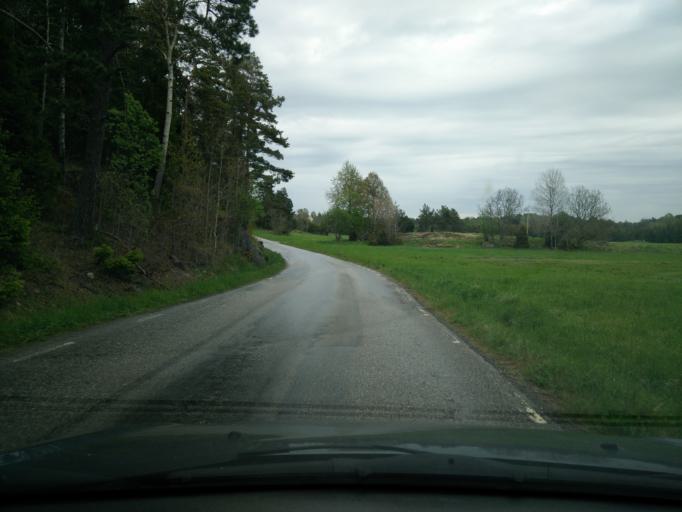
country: SE
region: Stockholm
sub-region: Norrtalje Kommun
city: Bjorko
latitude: 59.8219
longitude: 18.9050
